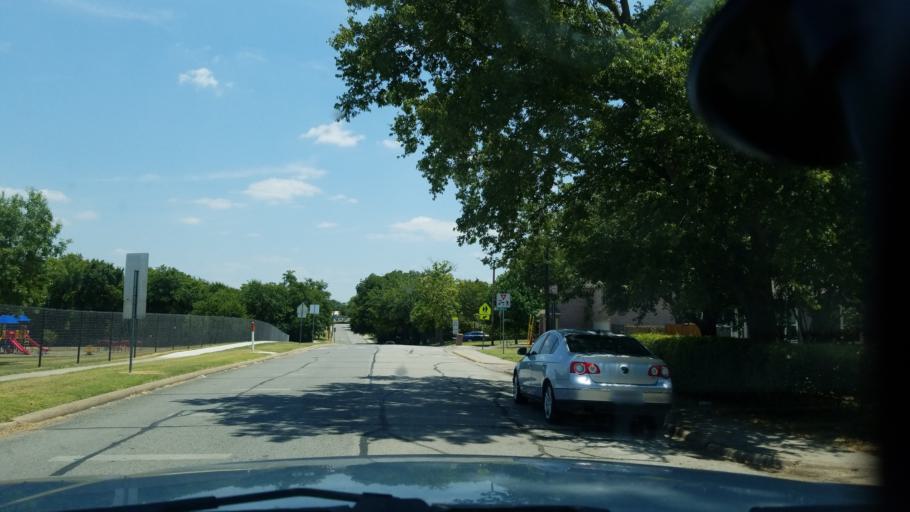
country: US
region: Texas
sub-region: Dallas County
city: Grand Prairie
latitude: 32.7557
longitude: -96.9693
